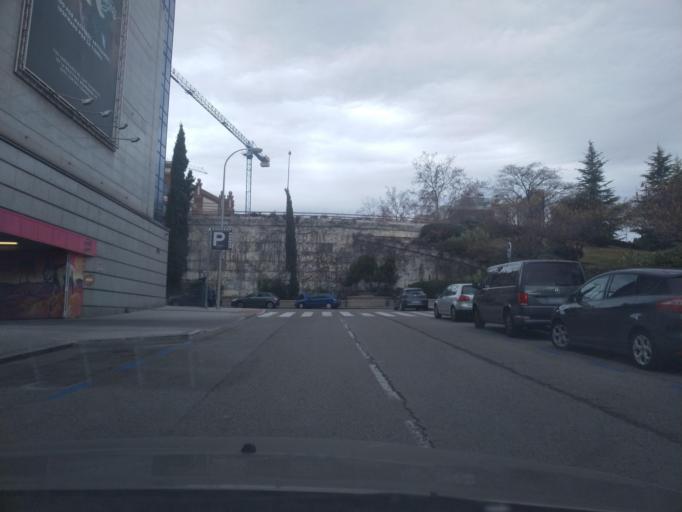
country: ES
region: Madrid
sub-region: Provincia de Madrid
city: Puente de Vallecas
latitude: 40.3955
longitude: -3.6748
